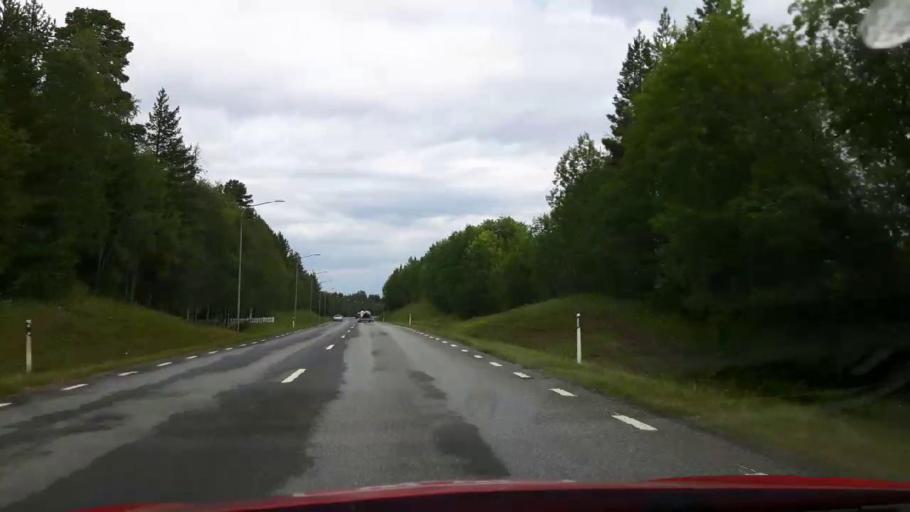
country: SE
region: Jaemtland
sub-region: Stroemsunds Kommun
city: Stroemsund
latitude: 63.6671
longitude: 15.3912
